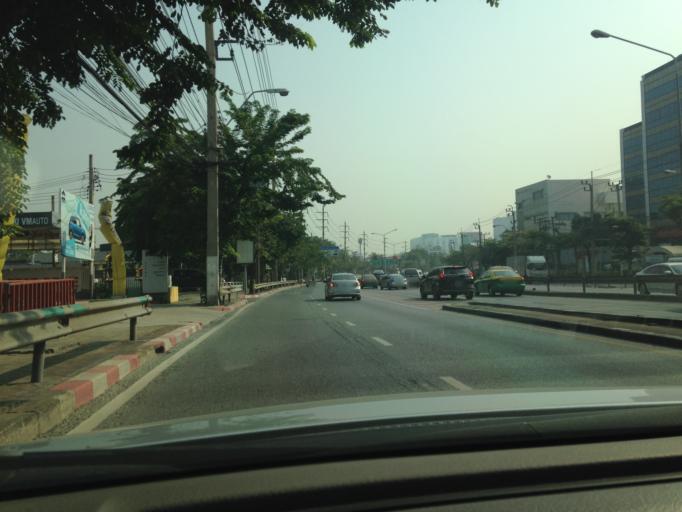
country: TH
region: Bangkok
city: Bang Sue
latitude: 13.8301
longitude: 100.5305
